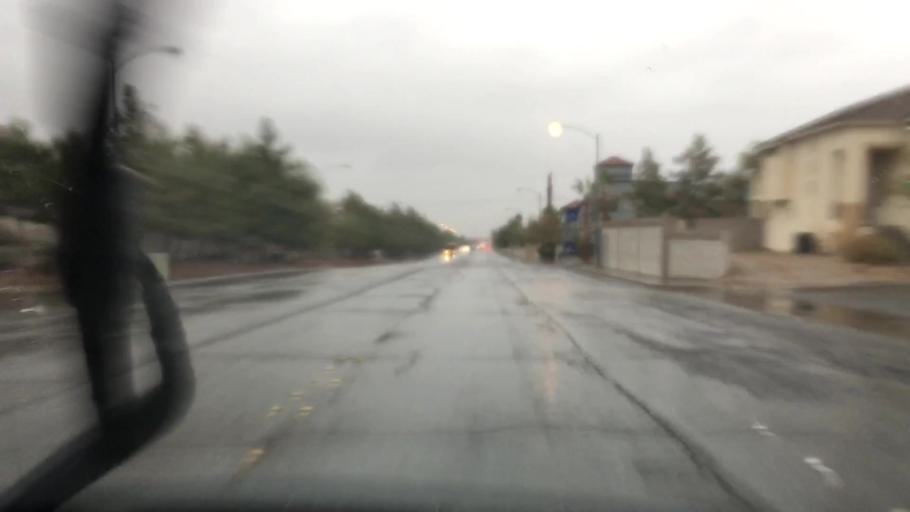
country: US
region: Nevada
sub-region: Clark County
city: Whitney
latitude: 36.0084
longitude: -115.1278
